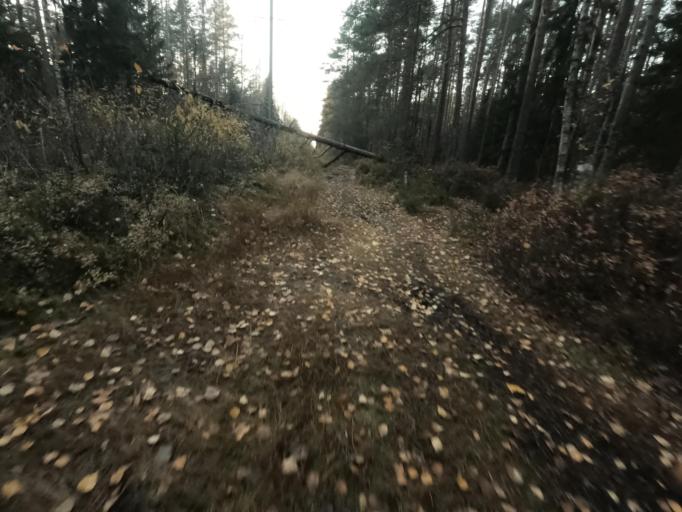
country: RU
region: St.-Petersburg
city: Komarovo
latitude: 60.2023
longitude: 29.8060
